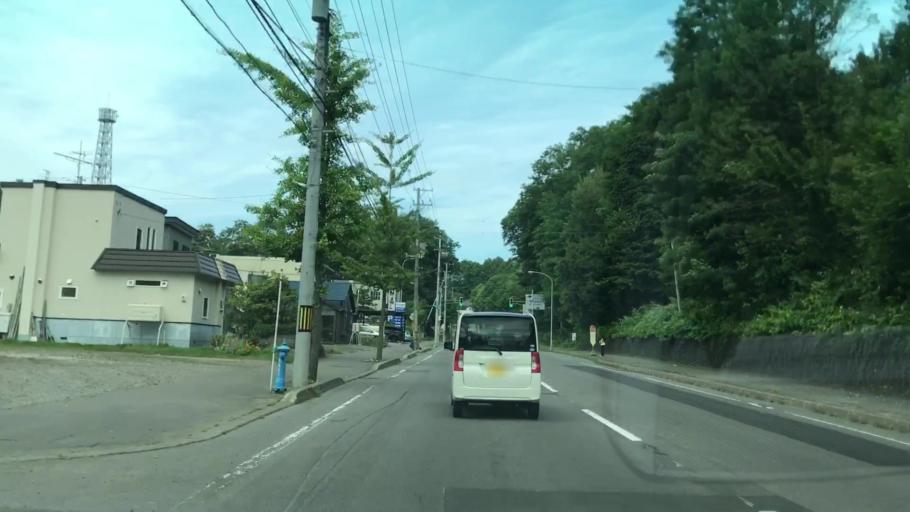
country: JP
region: Hokkaido
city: Otaru
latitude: 43.2105
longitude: 140.9684
